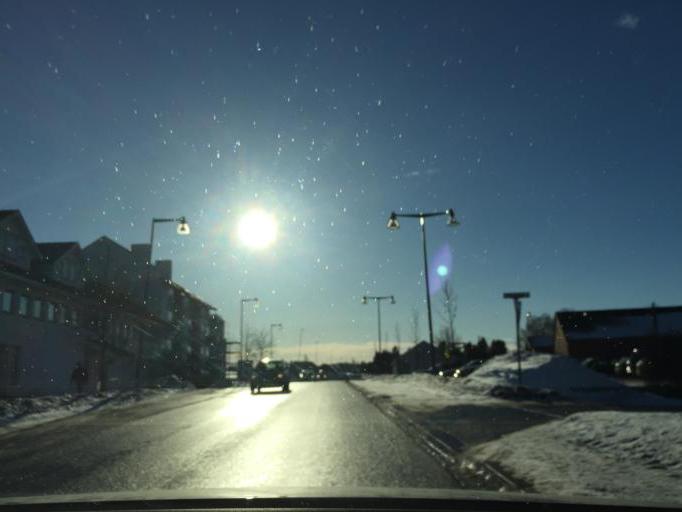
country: NO
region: Akershus
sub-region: Nes
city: Arnes
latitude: 60.1195
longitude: 11.4660
